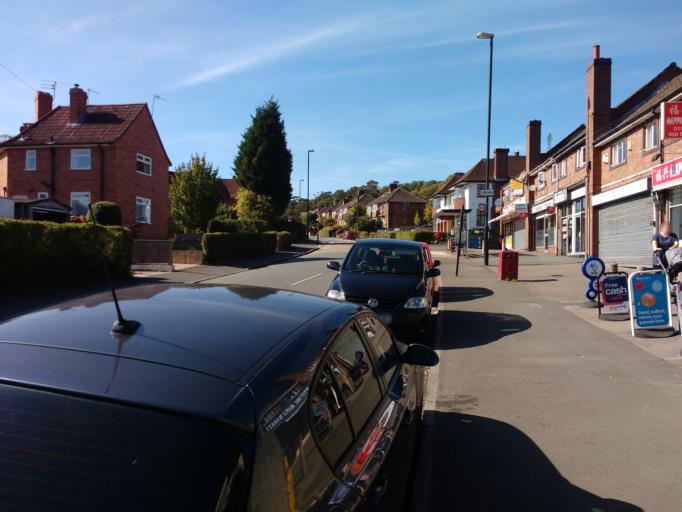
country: GB
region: England
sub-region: North Somerset
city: Easton-in-Gordano
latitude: 51.4937
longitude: -2.6470
